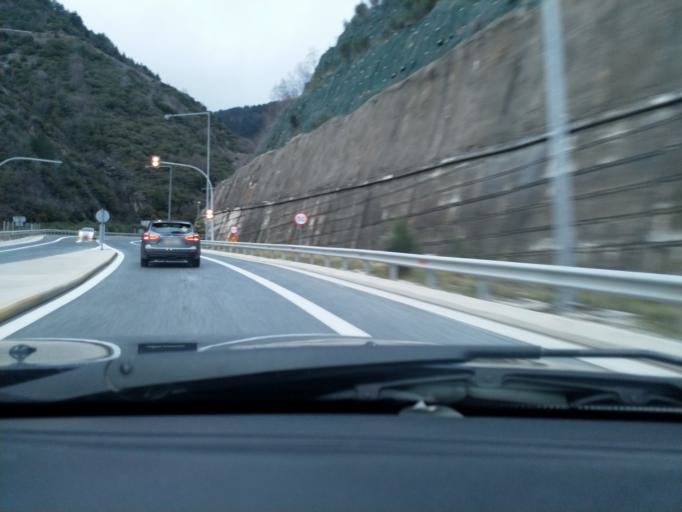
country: GR
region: Epirus
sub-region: Nomos Ioanninon
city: Metsovo
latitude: 39.7624
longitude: 21.1689
